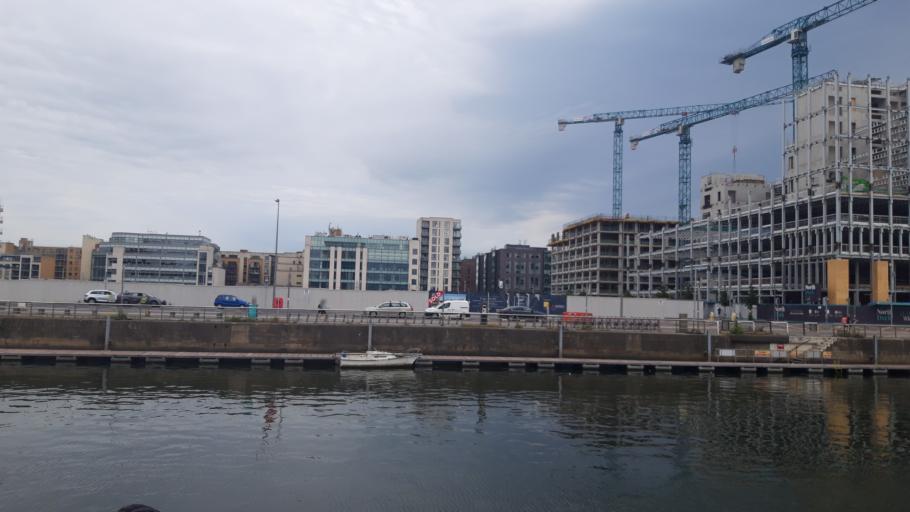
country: IE
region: Leinster
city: Ringsend
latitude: 53.3463
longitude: -6.2311
